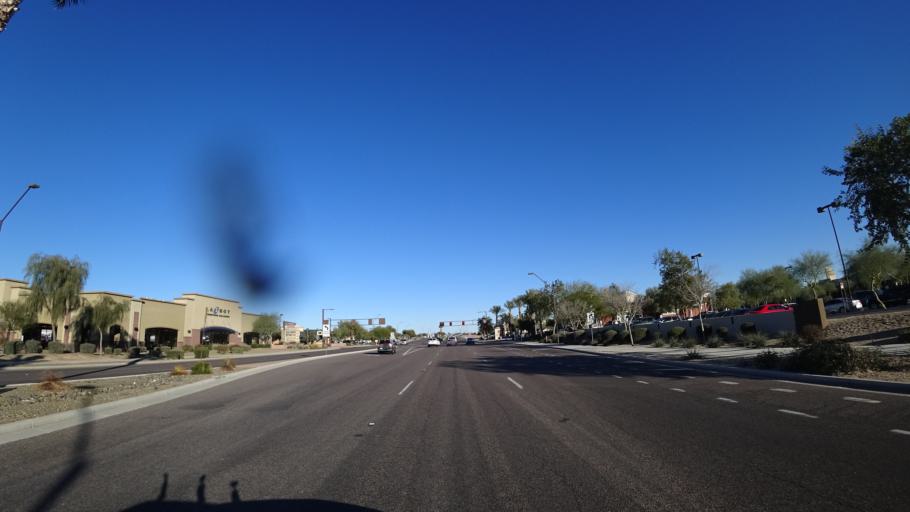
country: US
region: Arizona
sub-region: Maricopa County
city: Goodyear
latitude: 33.4644
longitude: -112.3893
